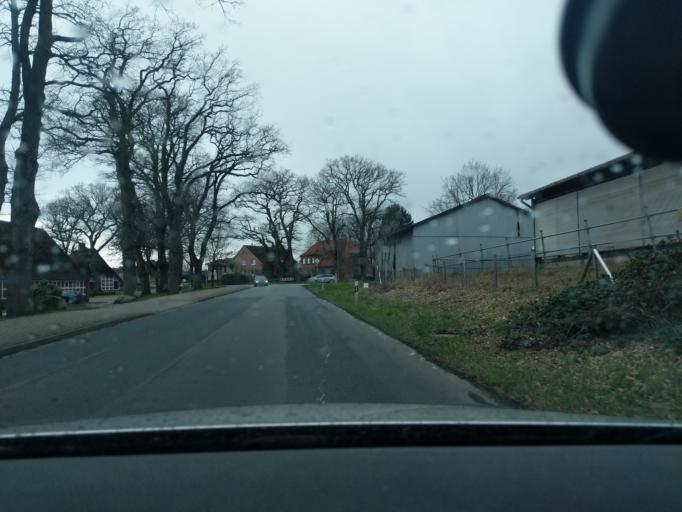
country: DE
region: Lower Saxony
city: Bargstedt
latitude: 53.4693
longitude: 9.4754
